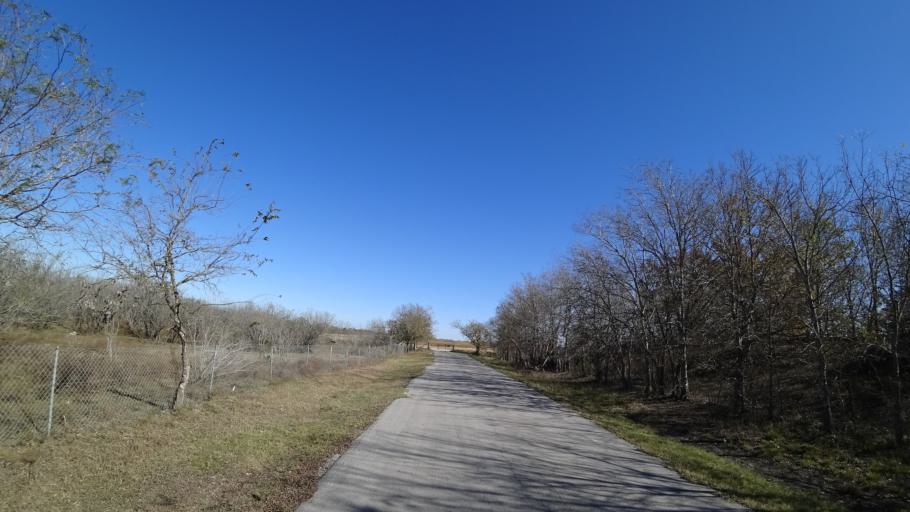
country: US
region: Texas
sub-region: Travis County
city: Garfield
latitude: 30.1148
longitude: -97.6219
